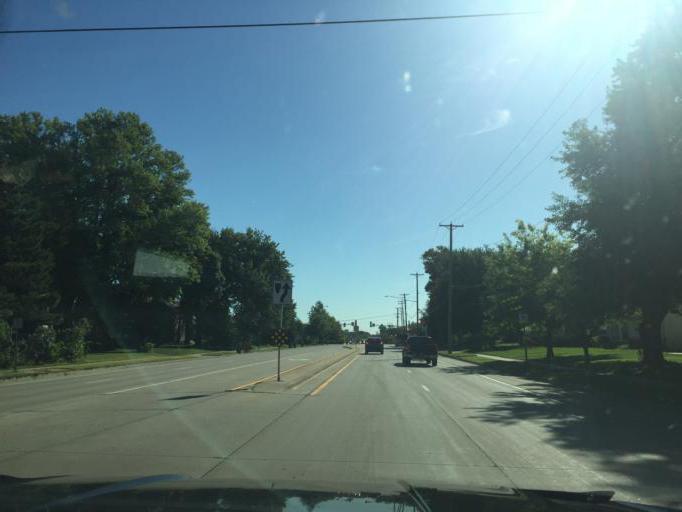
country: US
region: Minnesota
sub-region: Ramsey County
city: Falcon Heights
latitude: 44.9918
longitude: -93.1592
